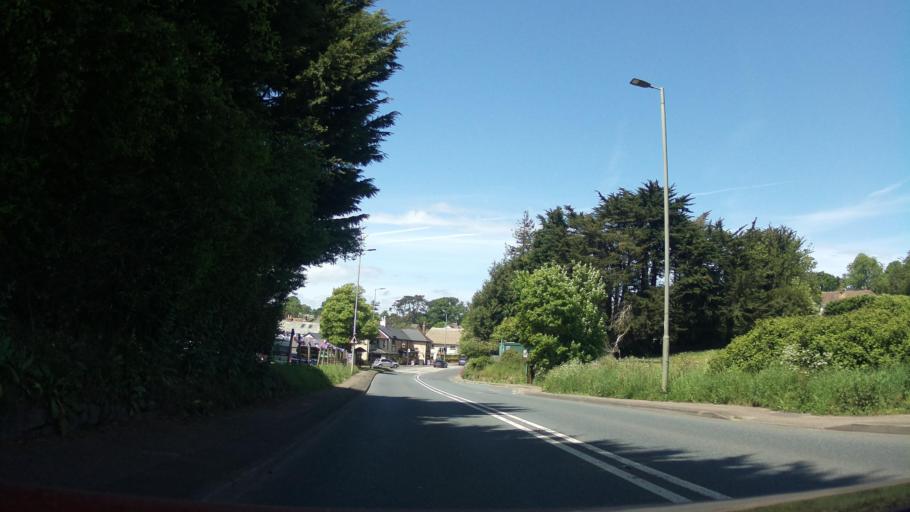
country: GB
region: England
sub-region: Devon
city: Exmouth
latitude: 50.6467
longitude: -3.4151
